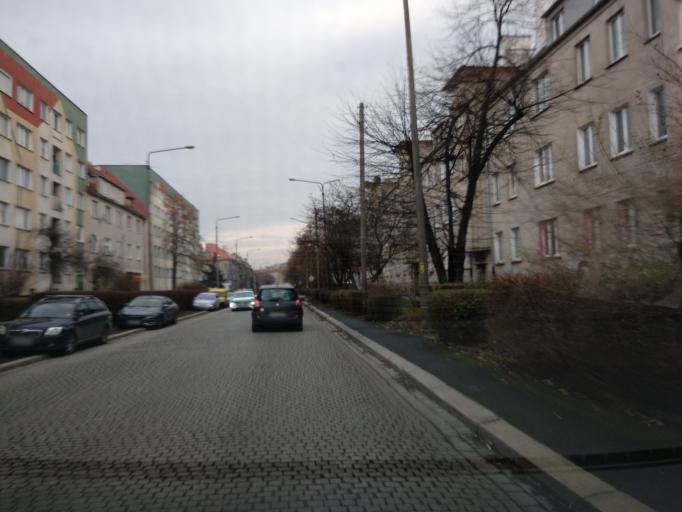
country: PL
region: Lower Silesian Voivodeship
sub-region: Powiat wroclawski
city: Wroclaw
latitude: 51.0938
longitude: 16.9985
